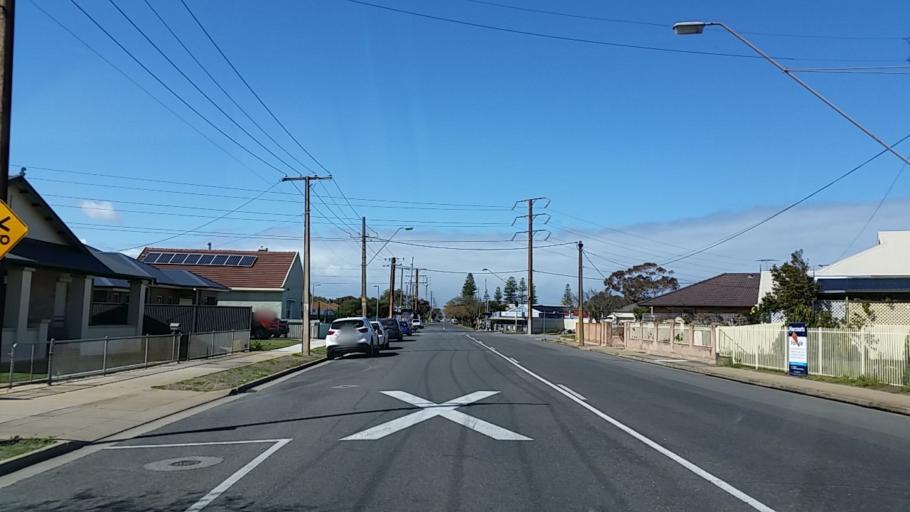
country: AU
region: South Australia
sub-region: Port Adelaide Enfield
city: Birkenhead
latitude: -34.8196
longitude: 138.4940
